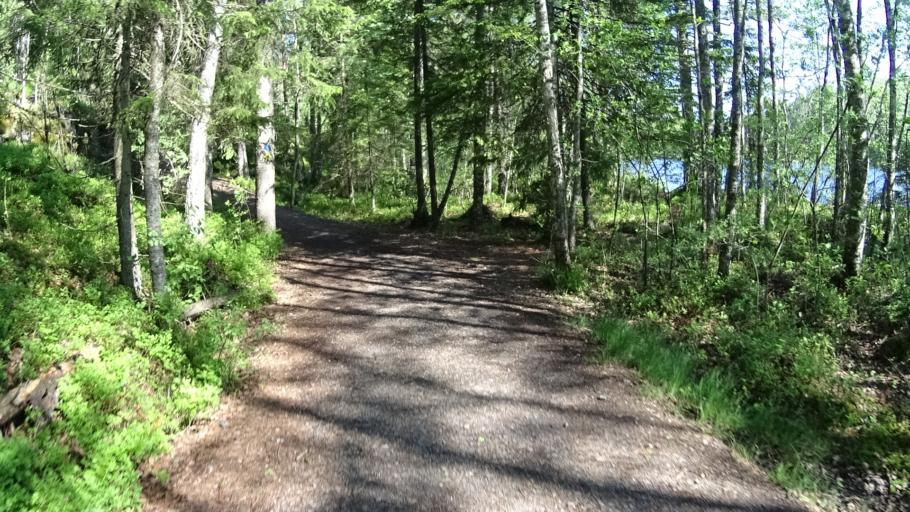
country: FI
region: Uusimaa
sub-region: Helsinki
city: Kauniainen
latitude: 60.3332
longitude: 24.6847
